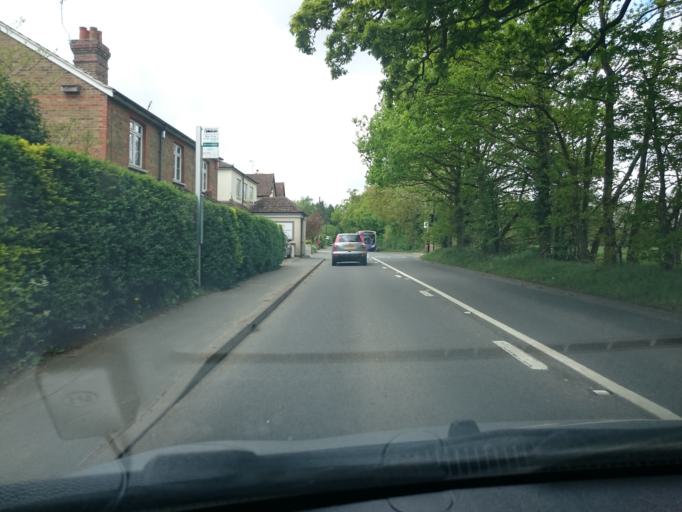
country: GB
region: England
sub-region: Surrey
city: Normandy
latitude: 51.2574
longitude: -0.6572
